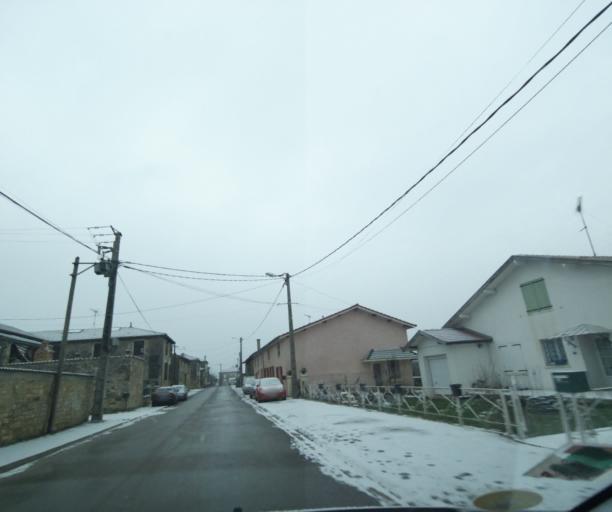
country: FR
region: Champagne-Ardenne
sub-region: Departement de la Haute-Marne
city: Wassy
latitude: 48.4732
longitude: 5.0355
